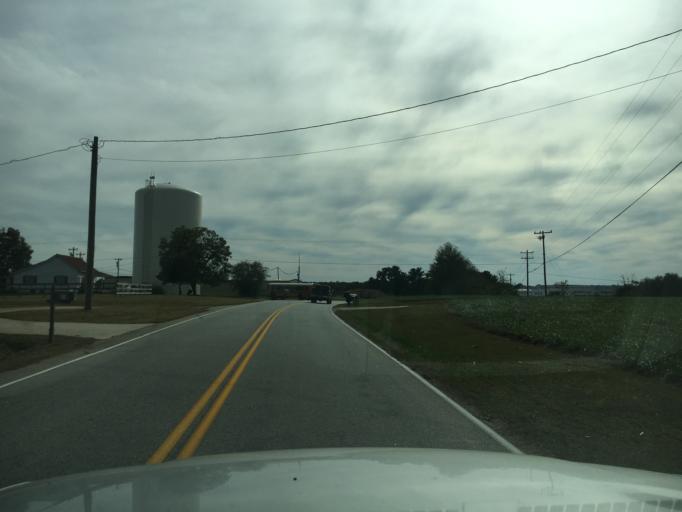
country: US
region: South Carolina
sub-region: Spartanburg County
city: Duncan
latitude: 34.9198
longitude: -82.1588
